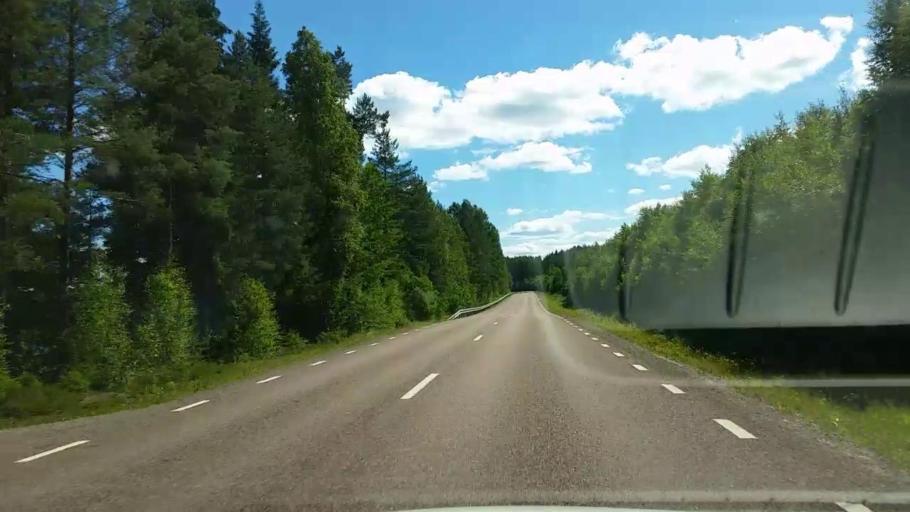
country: SE
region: Dalarna
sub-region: Faluns Kommun
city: Svardsjo
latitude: 60.9630
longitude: 15.6919
